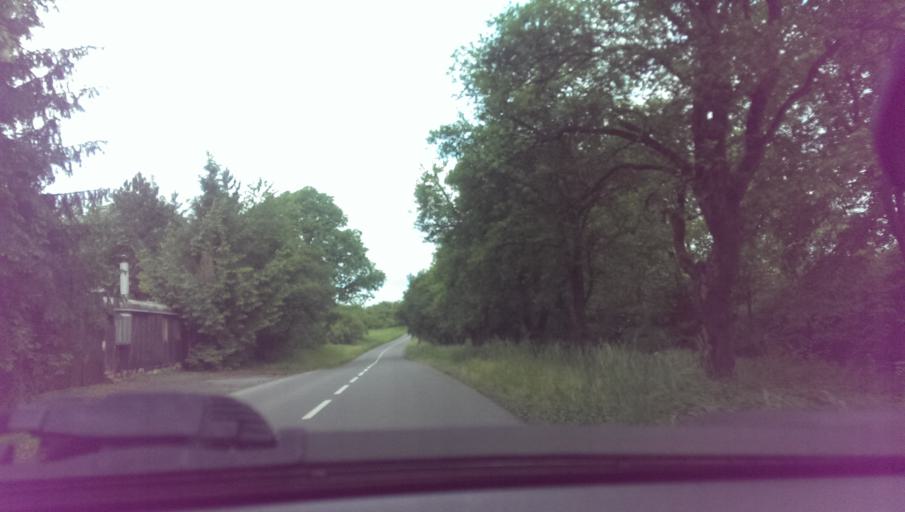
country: CZ
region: Zlin
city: Kvasice
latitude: 49.2331
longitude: 17.4845
